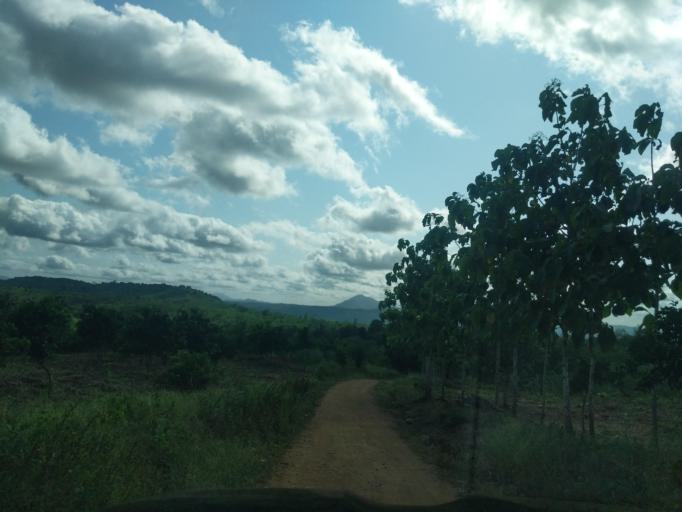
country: TZ
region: Tanga
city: Muheza
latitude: -5.4203
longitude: 38.6421
